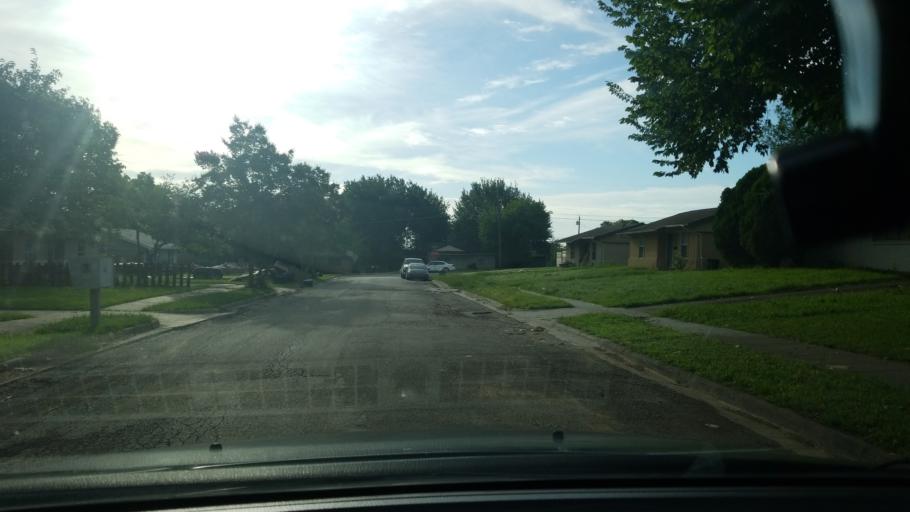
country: US
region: Texas
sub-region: Dallas County
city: Mesquite
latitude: 32.7572
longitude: -96.6244
